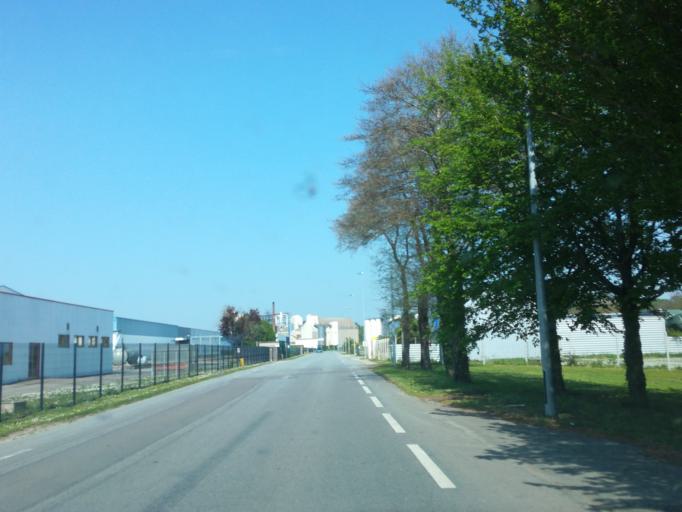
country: FR
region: Brittany
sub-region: Departement du Morbihan
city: Le Sourn
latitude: 48.0435
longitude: -2.9648
